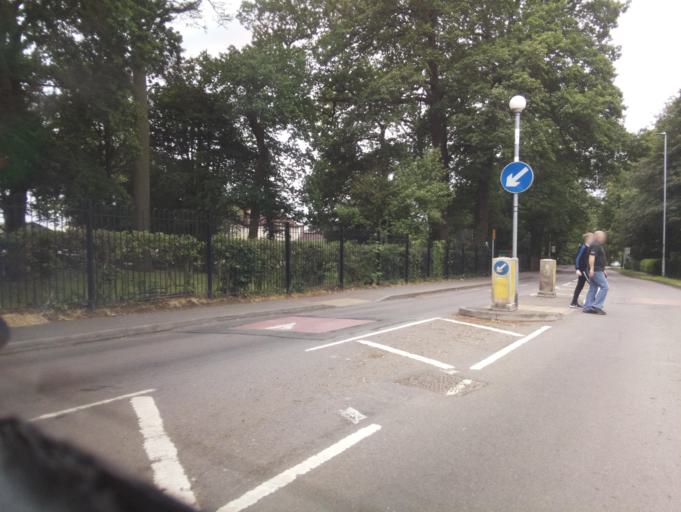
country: GB
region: England
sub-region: Leicestershire
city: Coalville
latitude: 52.7232
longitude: -1.3483
